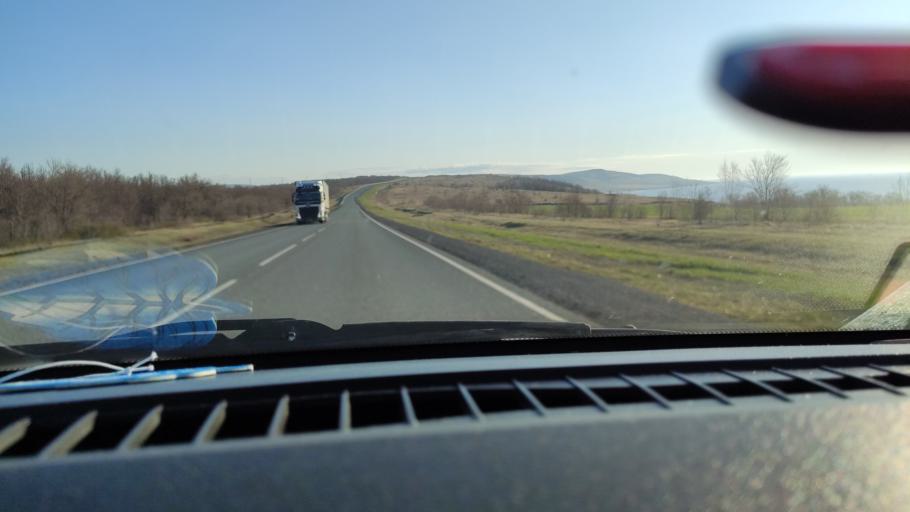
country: RU
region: Saratov
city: Balakovo
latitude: 52.1956
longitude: 47.8583
